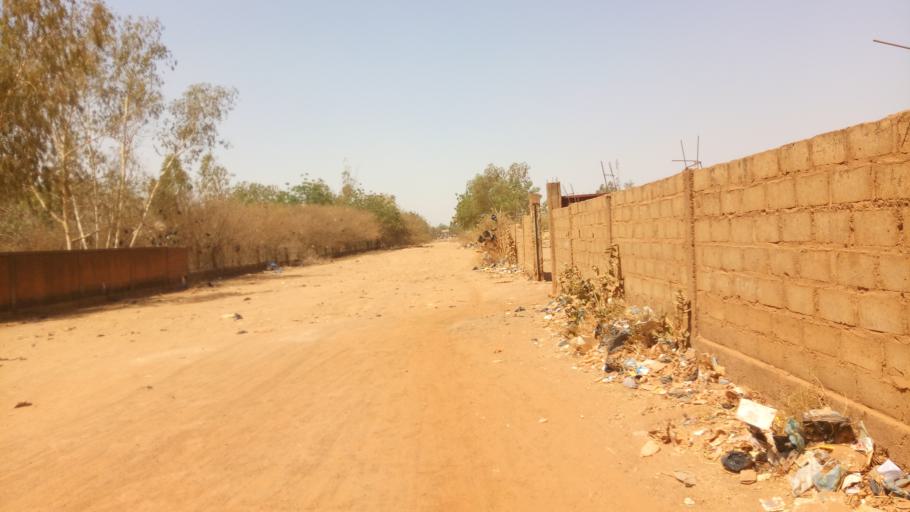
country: BF
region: Centre
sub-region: Kadiogo Province
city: Ouagadougou
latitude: 12.3938
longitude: -1.5690
